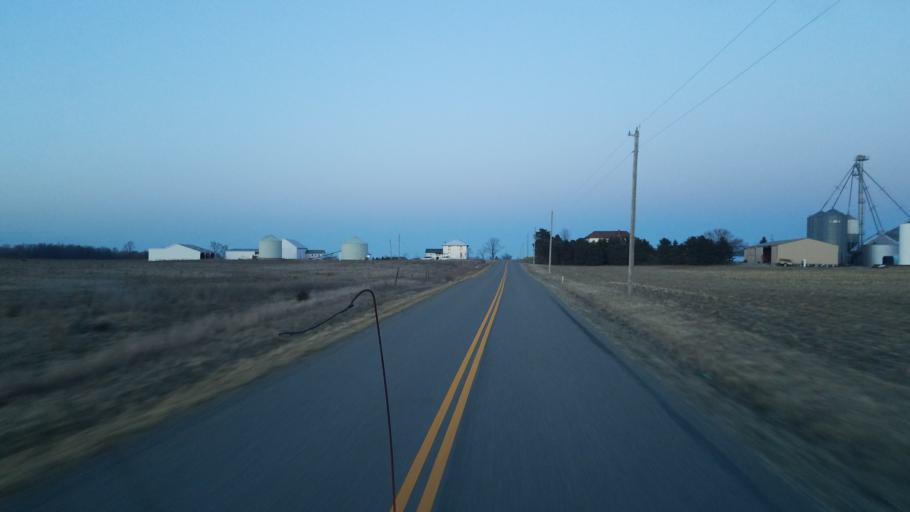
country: US
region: Ohio
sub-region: Champaign County
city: North Lewisburg
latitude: 40.2372
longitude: -83.6162
